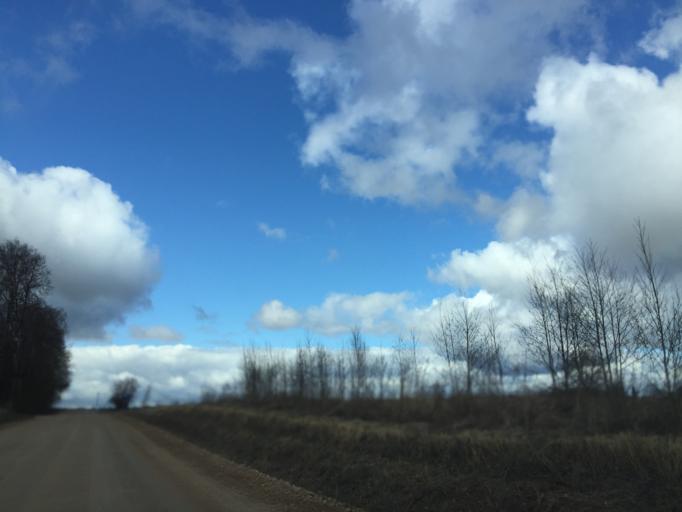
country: LV
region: Akniste
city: Akniste
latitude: 56.1130
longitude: 25.8681
